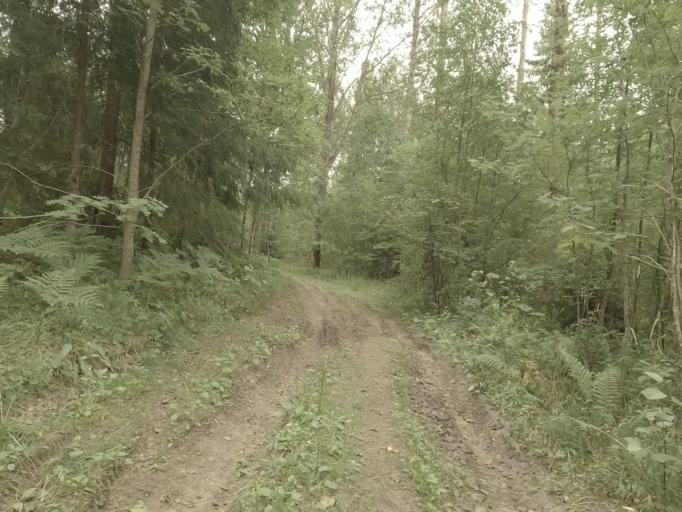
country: RU
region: Leningrad
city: Kamennogorsk
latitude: 61.0749
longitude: 29.1571
